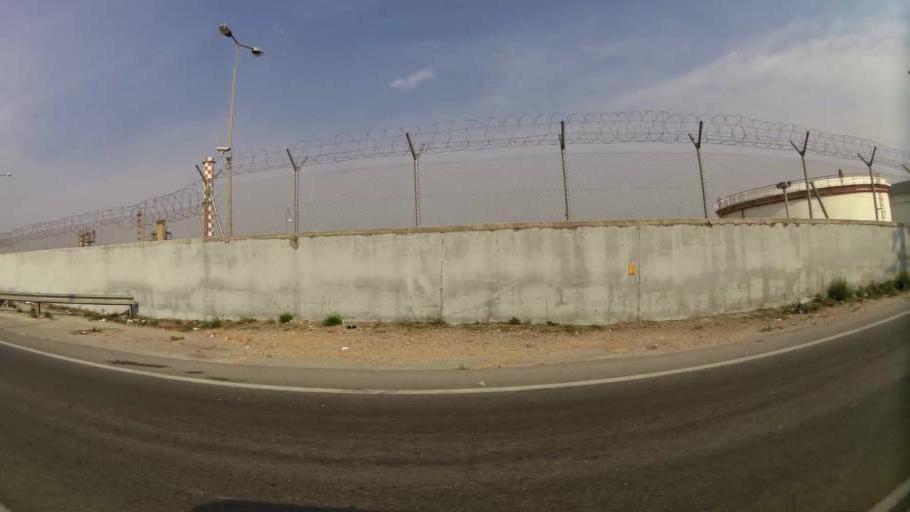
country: GR
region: Attica
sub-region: Nomarchia Athinas
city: Skaramangas
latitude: 38.0291
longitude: 23.6093
